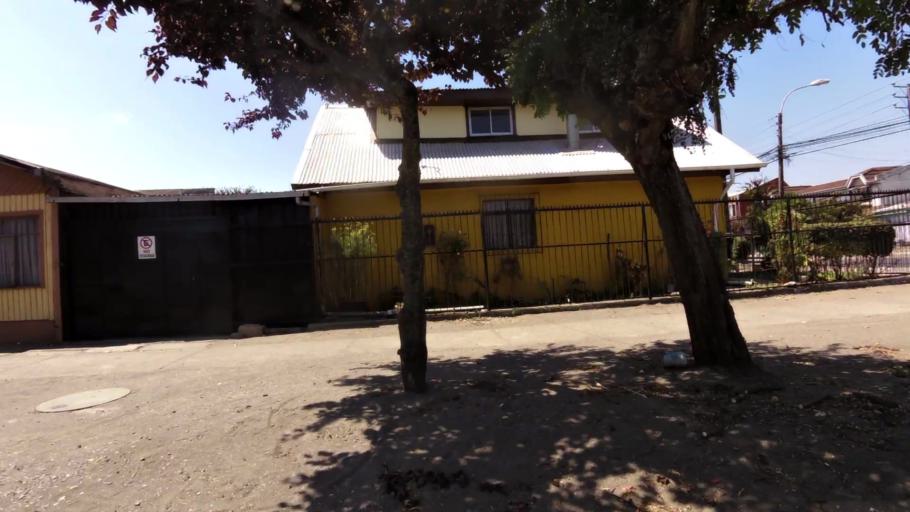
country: CL
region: Biobio
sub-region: Provincia de Concepcion
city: Concepcion
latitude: -36.8100
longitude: -73.0520
